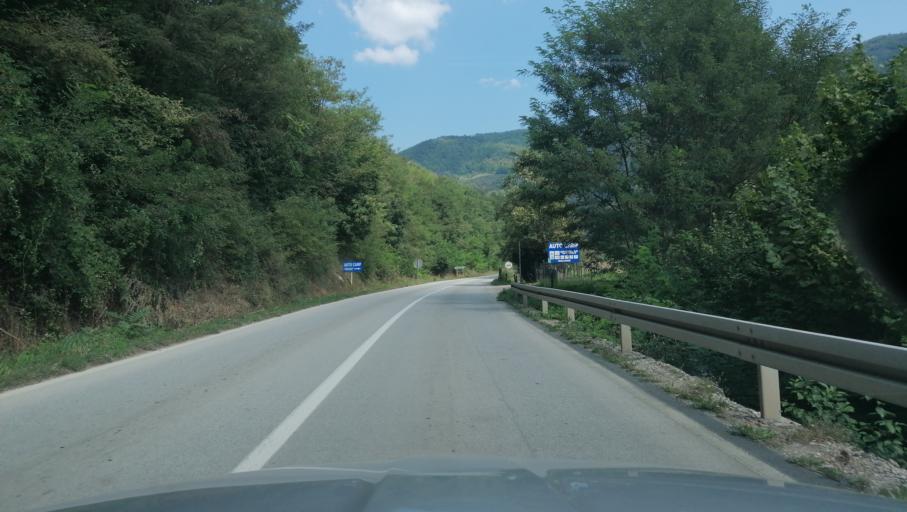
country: BA
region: Republika Srpska
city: Foca
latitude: 43.5295
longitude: 18.7826
